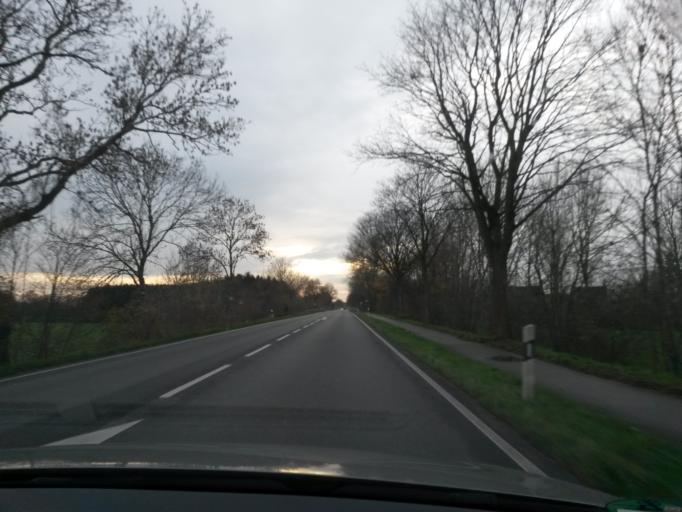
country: DE
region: North Rhine-Westphalia
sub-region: Regierungsbezirk Dusseldorf
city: Alpen
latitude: 51.6005
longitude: 6.5444
